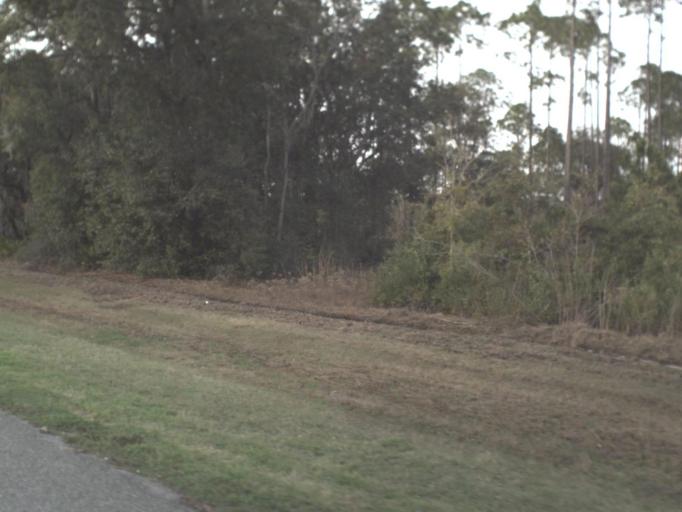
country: US
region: Florida
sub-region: Bay County
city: Tyndall Air Force Base
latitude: 30.0398
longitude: -85.5510
